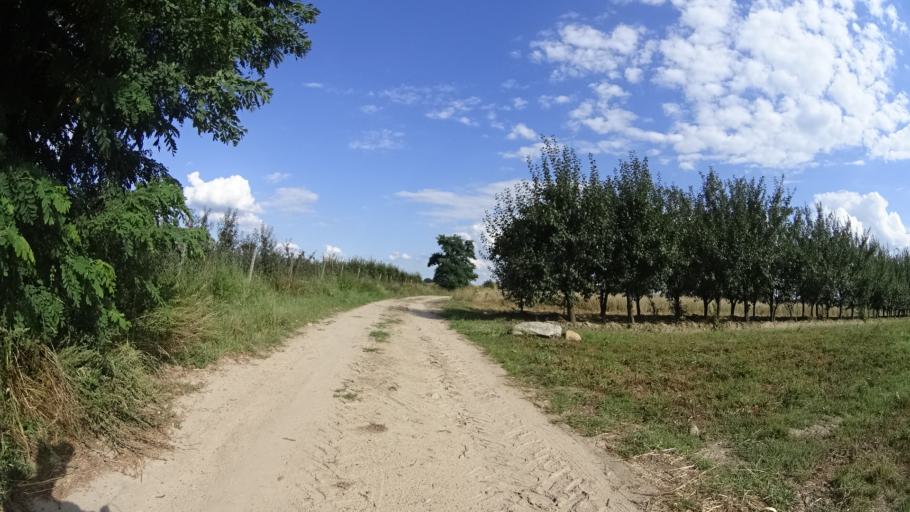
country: PL
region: Masovian Voivodeship
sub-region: Powiat bialobrzeski
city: Wysmierzyce
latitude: 51.6752
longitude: 20.7896
